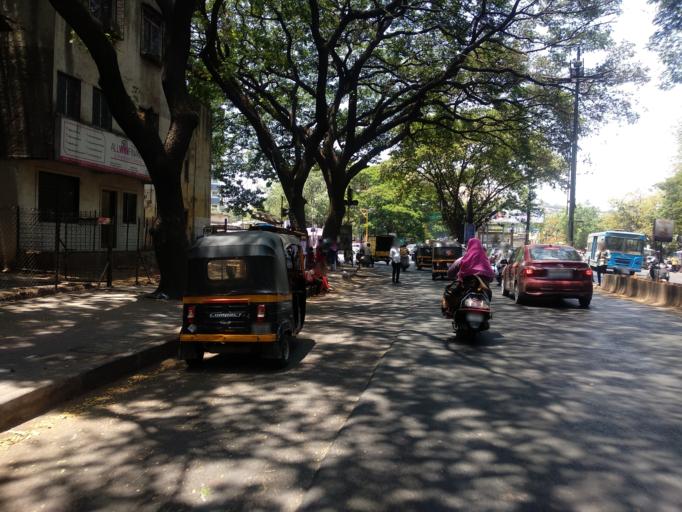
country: IN
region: Maharashtra
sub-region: Pune Division
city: Pune
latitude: 18.5037
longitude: 73.8454
